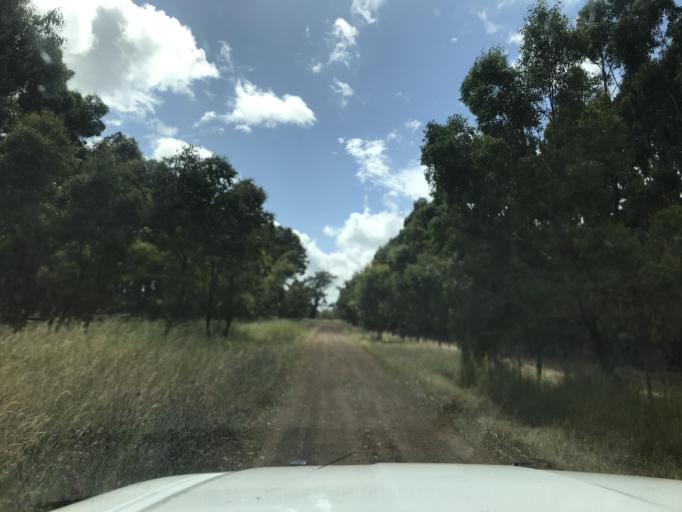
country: AU
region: South Australia
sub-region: Wattle Range
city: Penola
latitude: -37.1907
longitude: 141.3862
